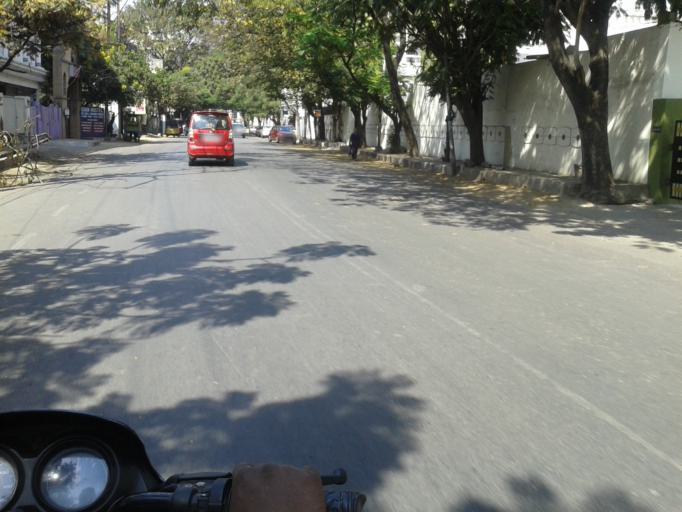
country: IN
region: Telangana
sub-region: Hyderabad
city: Hyderabad
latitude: 17.3917
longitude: 78.4845
